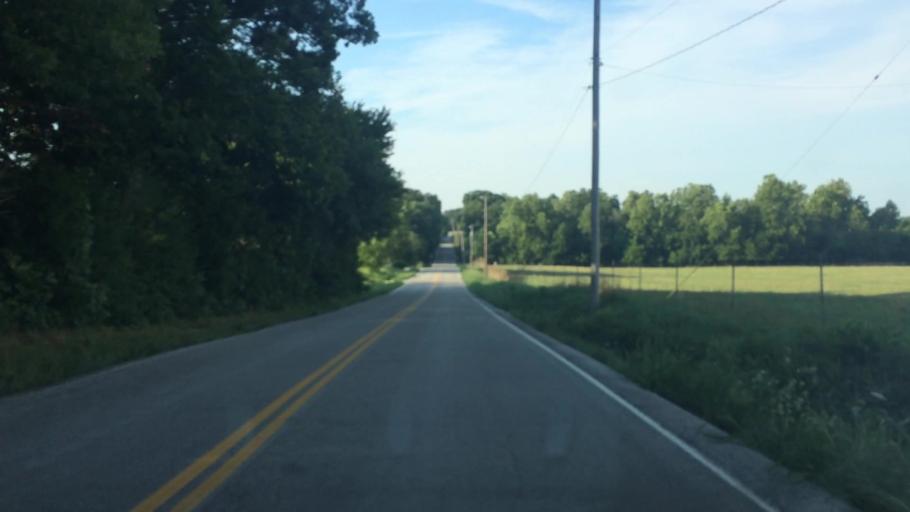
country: US
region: Missouri
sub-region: Greene County
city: Strafford
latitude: 37.2617
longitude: -93.1878
